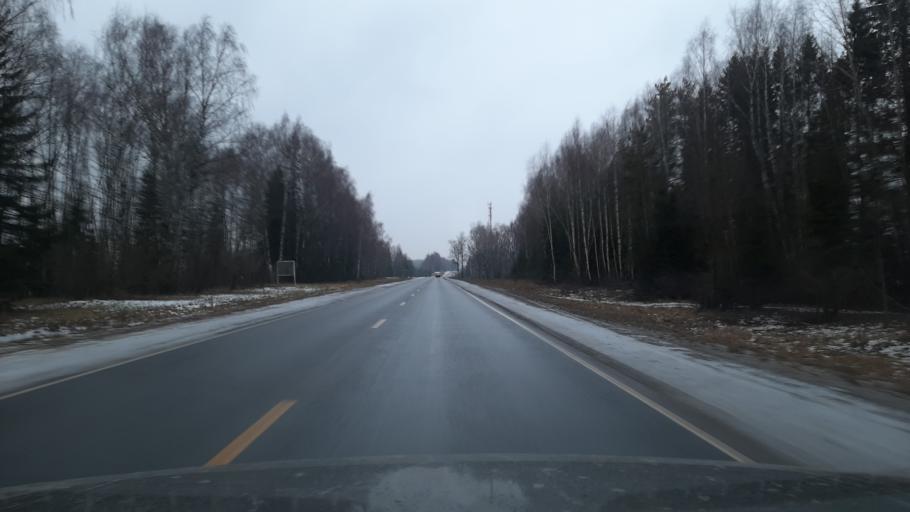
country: RU
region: Ivanovo
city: Kitovo
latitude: 56.8896
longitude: 41.2194
